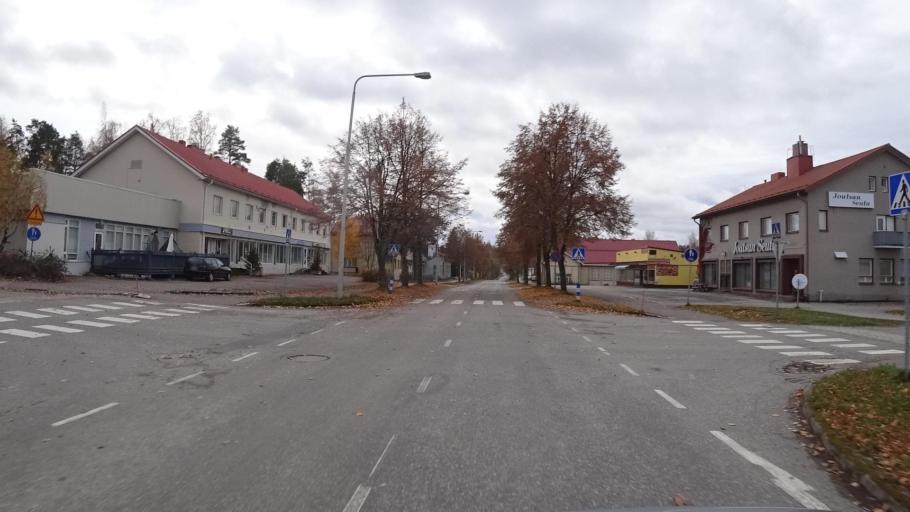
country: FI
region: Central Finland
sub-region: Joutsa
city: Joutsa
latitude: 61.7404
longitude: 26.1132
